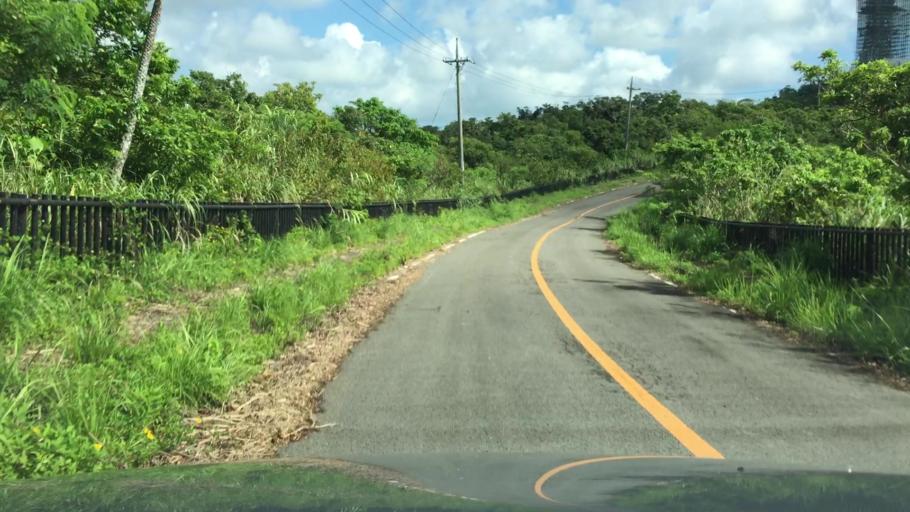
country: JP
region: Okinawa
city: Ishigaki
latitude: 24.3753
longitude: 124.1640
